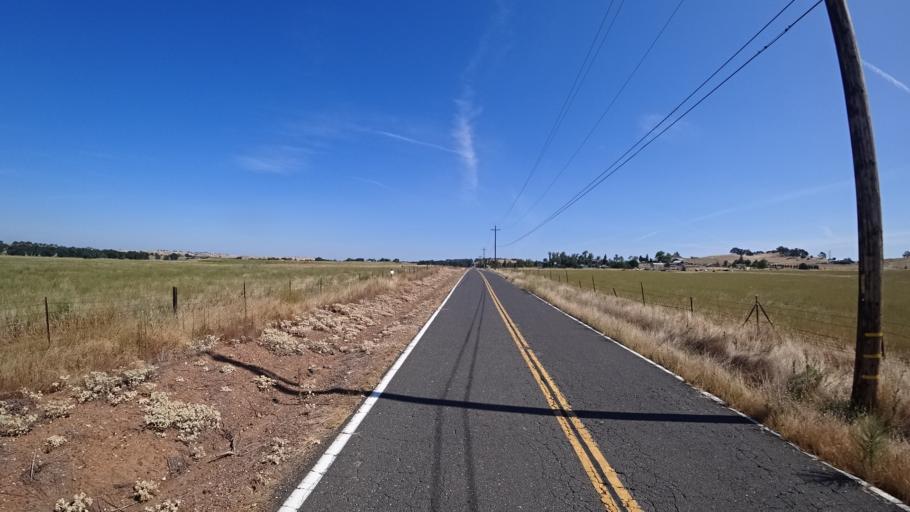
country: US
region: California
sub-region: Calaveras County
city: Rancho Calaveras
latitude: 38.0818
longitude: -120.9264
